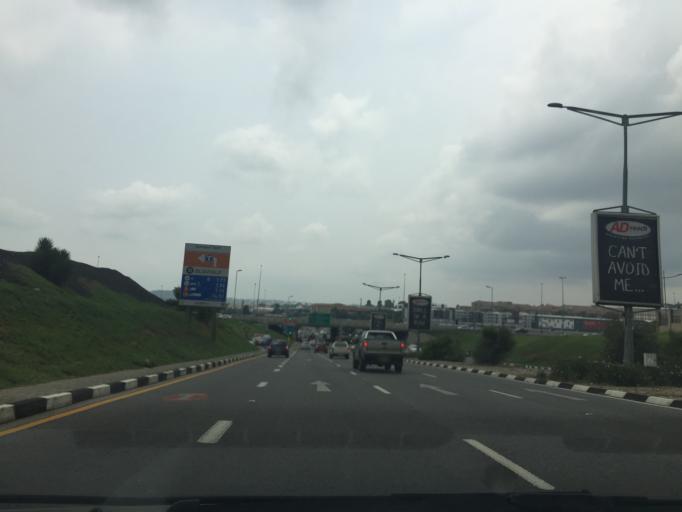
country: ZA
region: Gauteng
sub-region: City of Johannesburg Metropolitan Municipality
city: Midrand
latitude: -26.0405
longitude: 28.0603
